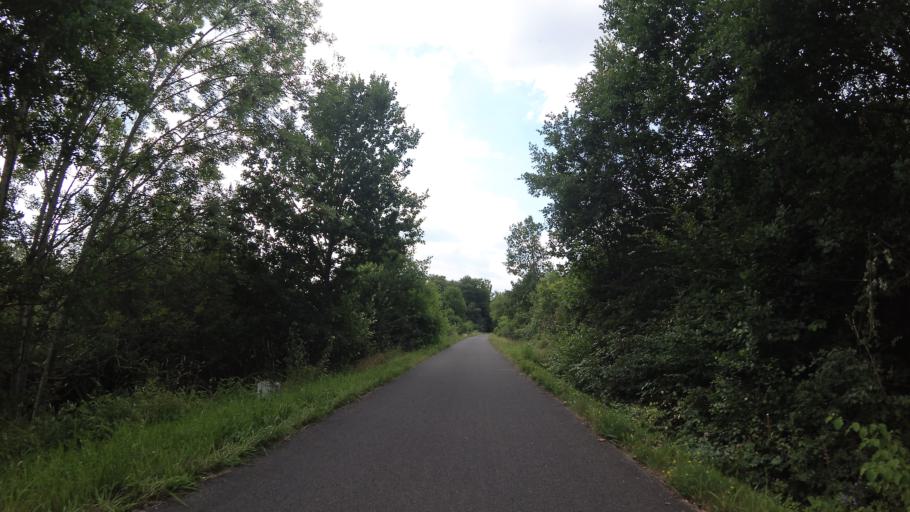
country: DE
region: Saarland
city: Blieskastel
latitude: 49.2283
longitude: 7.2598
